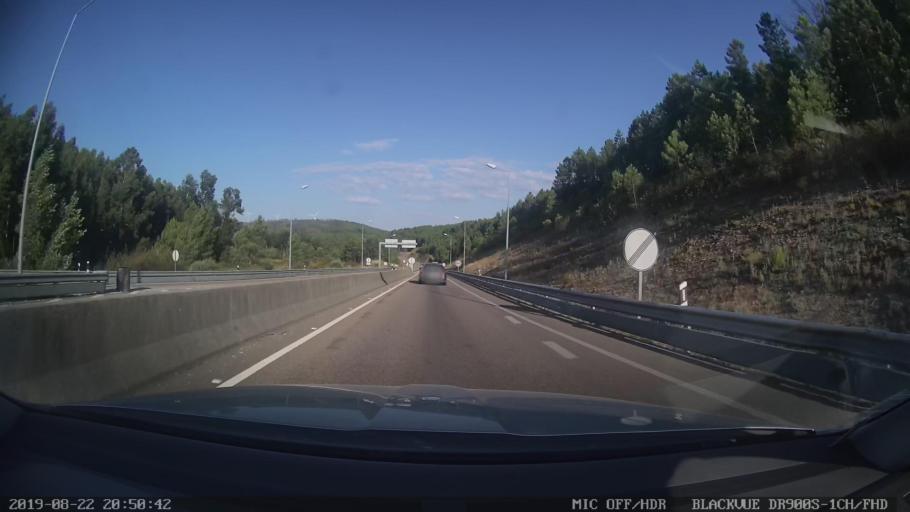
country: PT
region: Castelo Branco
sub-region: Proenca-A-Nova
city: Proenca-a-Nova
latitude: 39.7566
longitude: -7.9437
